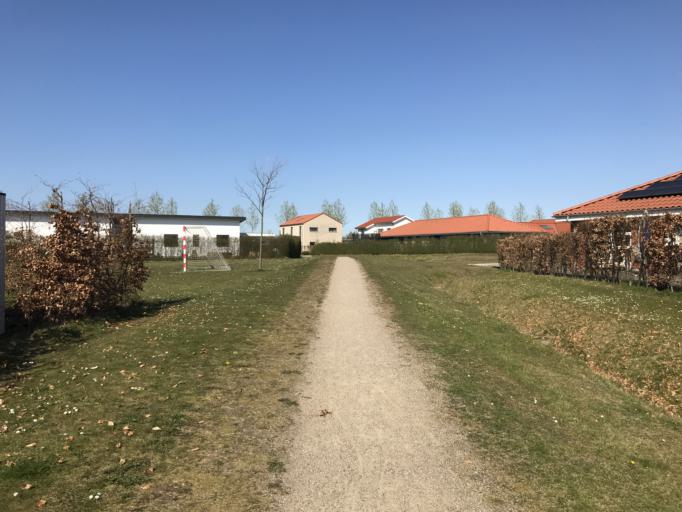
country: DK
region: Capital Region
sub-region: Hoje-Taastrup Kommune
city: Flong
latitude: 55.6602
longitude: 12.1503
